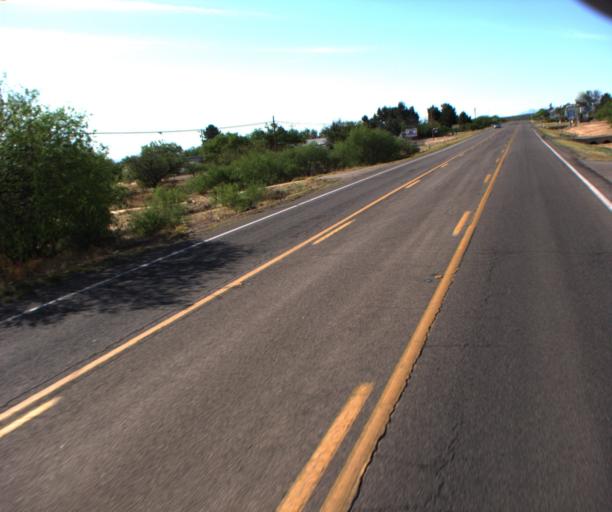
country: US
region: Arizona
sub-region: Cochise County
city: Benson
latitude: 31.9524
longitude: -110.2860
